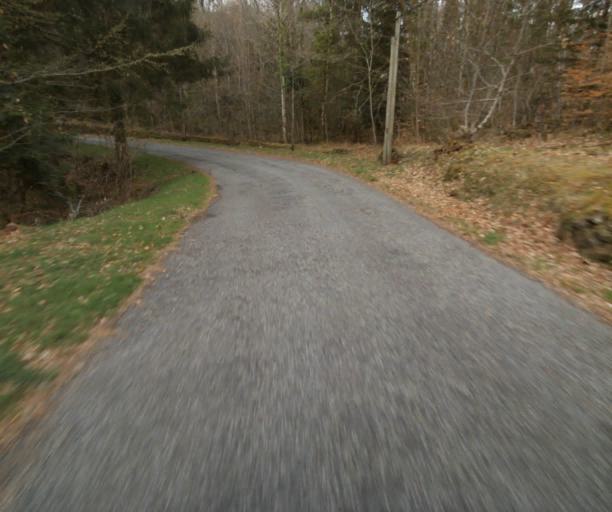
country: FR
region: Limousin
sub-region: Departement de la Correze
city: Argentat
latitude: 45.2502
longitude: 1.9755
